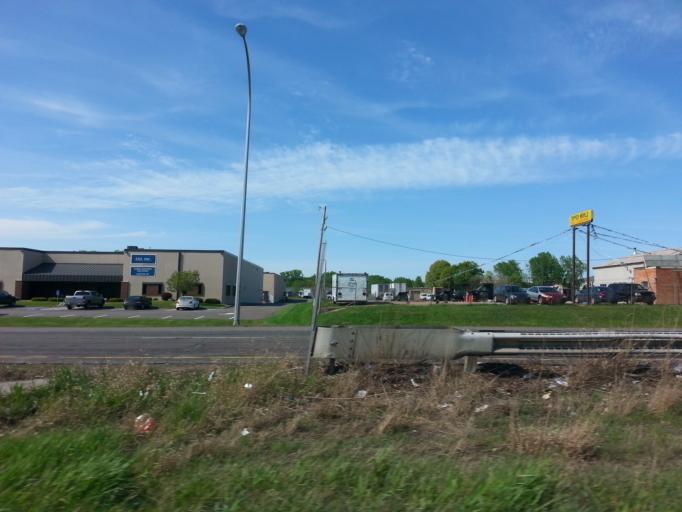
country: US
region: Minnesota
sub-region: Ramsey County
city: North Saint Paul
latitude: 45.0116
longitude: -93.0261
